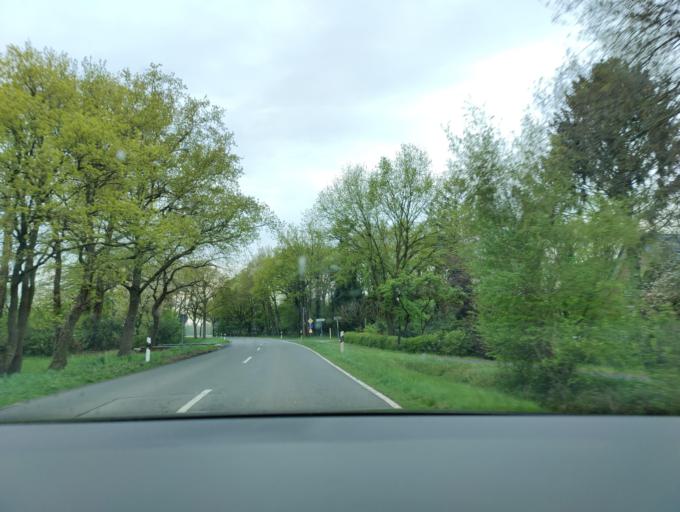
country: DE
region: Lower Saxony
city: Wietmarschen
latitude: 52.5101
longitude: 7.1563
